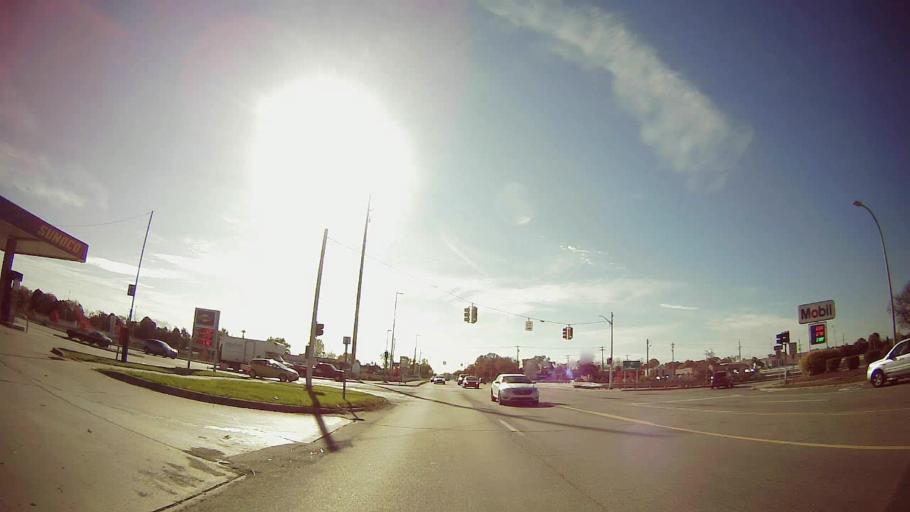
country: US
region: Michigan
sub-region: Wayne County
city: Livonia
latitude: 42.3833
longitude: -83.3728
